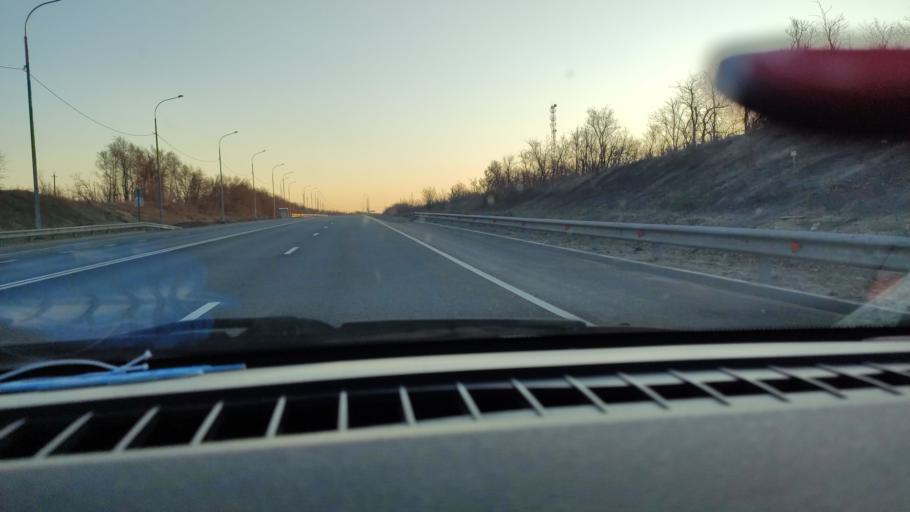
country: RU
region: Saratov
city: Yelshanka
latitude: 51.8913
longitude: 46.5247
